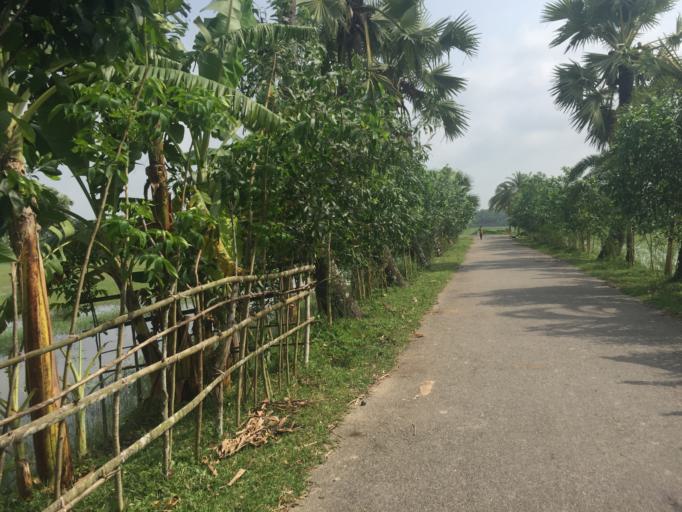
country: BD
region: Barisal
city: Mathba
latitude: 22.2545
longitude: 89.9125
